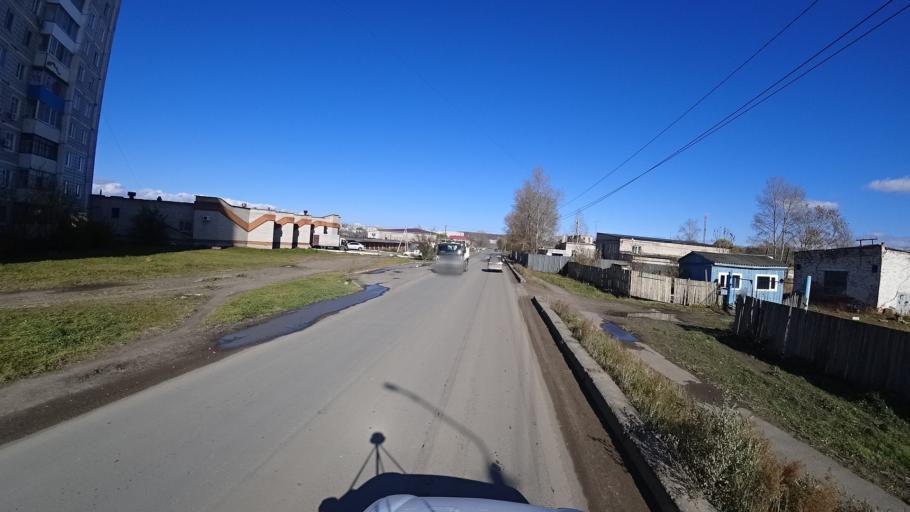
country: RU
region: Khabarovsk Krai
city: Amursk
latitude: 50.2185
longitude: 136.8951
